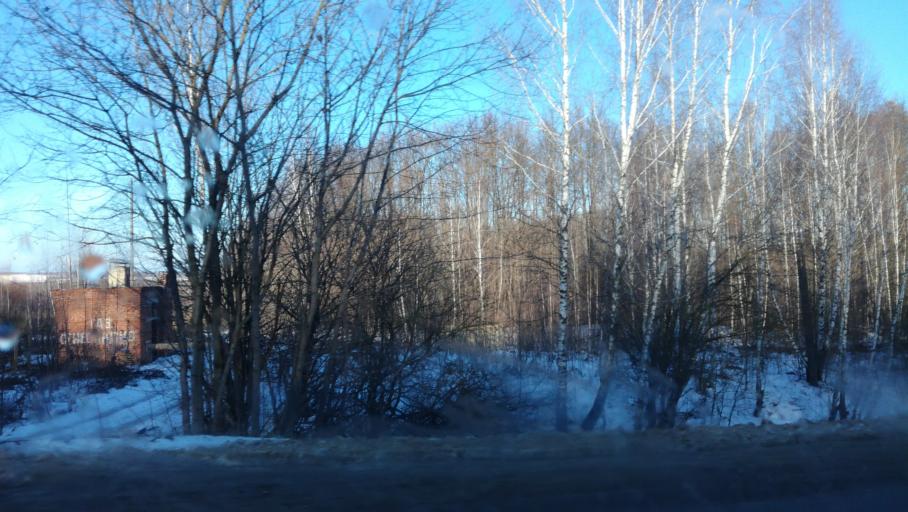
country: RU
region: Tula
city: Kosaya Gora
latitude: 54.1728
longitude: 37.4923
